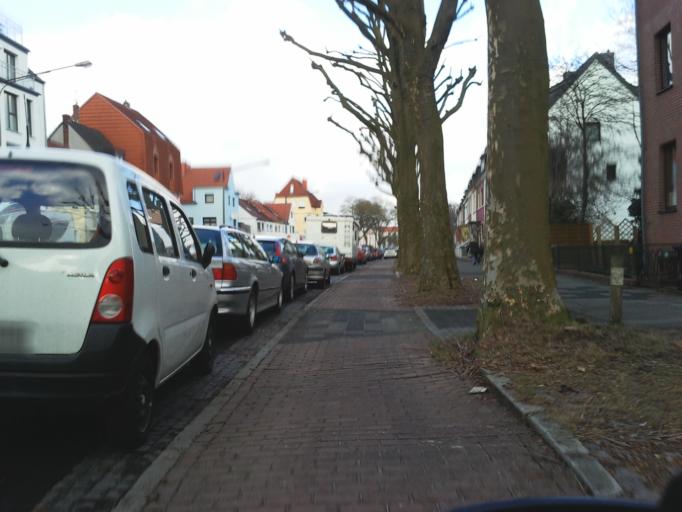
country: DE
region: Bremen
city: Bremen
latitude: 53.0966
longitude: 8.8070
